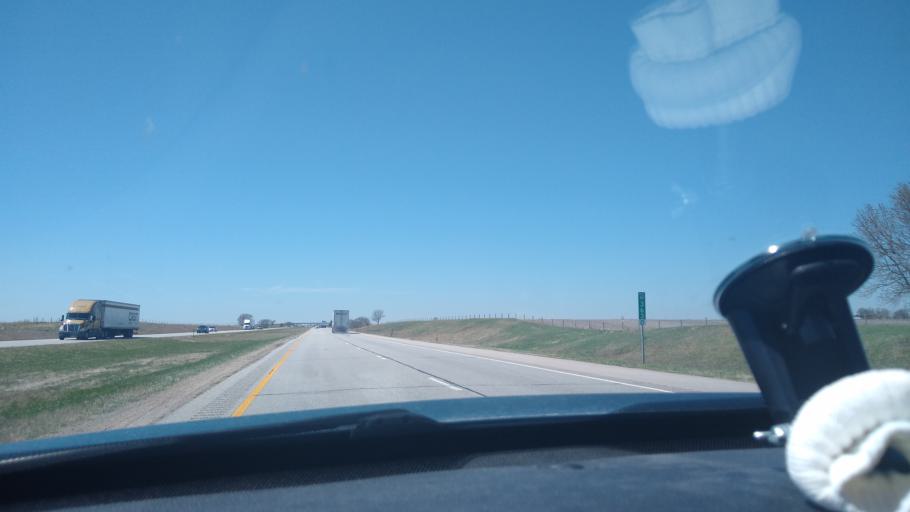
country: US
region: Nebraska
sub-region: York County
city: York
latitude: 40.8213
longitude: -97.4087
